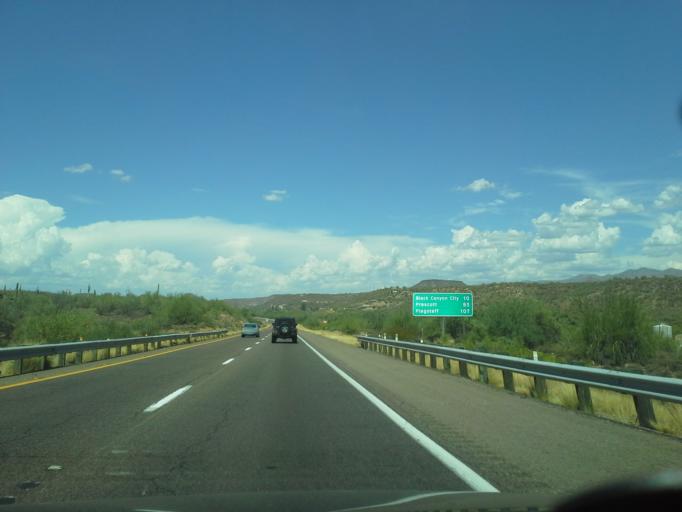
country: US
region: Arizona
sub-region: Maricopa County
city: New River
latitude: 33.9275
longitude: -112.1418
